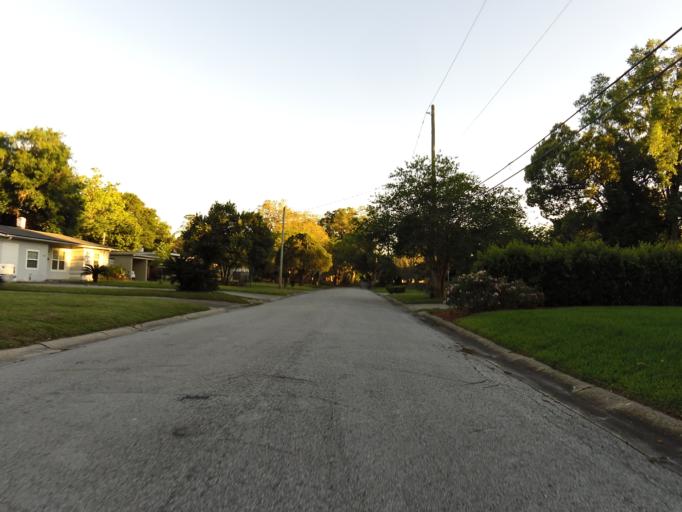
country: US
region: Florida
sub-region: Duval County
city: Jacksonville
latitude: 30.2598
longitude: -81.6395
